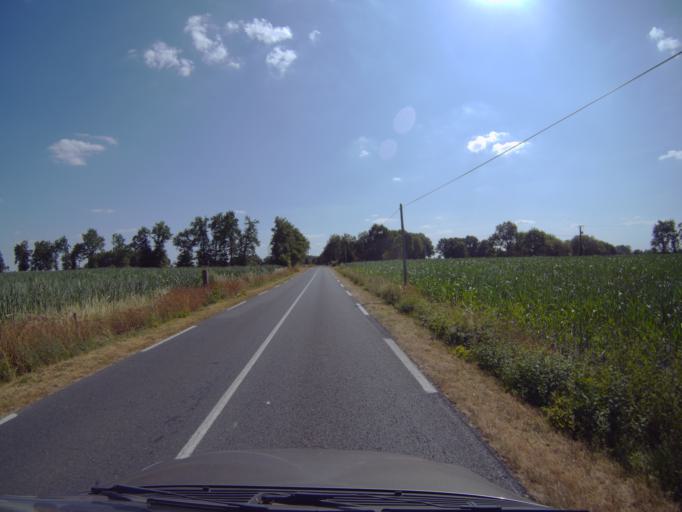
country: FR
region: Pays de la Loire
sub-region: Departement de la Loire-Atlantique
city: Aigrefeuille-sur-Maine
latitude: 47.0628
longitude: -1.4390
